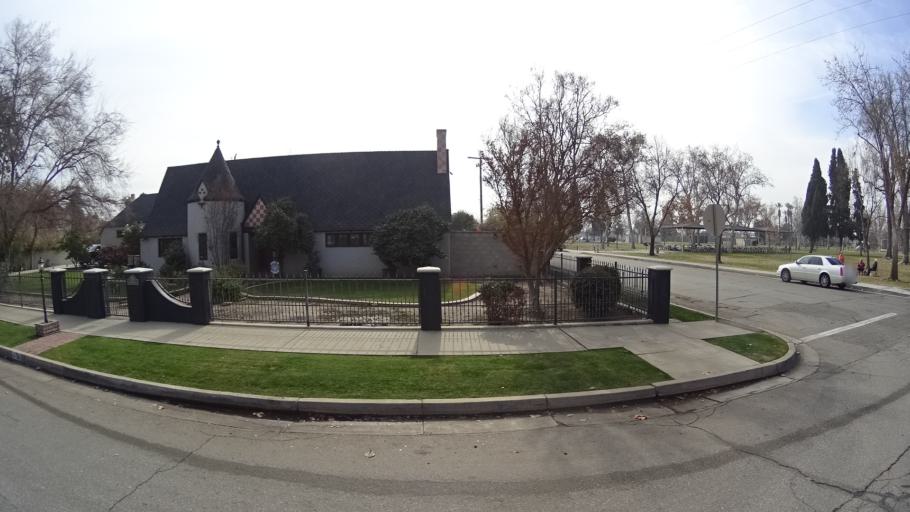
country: US
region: California
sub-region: Kern County
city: Bakersfield
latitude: 35.3753
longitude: -119.0339
